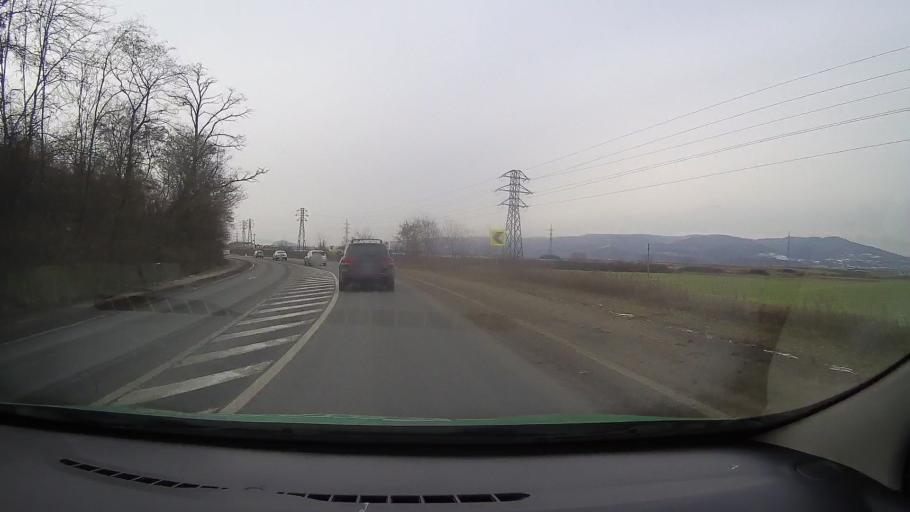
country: RO
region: Hunedoara
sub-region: Comuna Turdas
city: Pricaz
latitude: 45.8415
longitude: 23.1681
